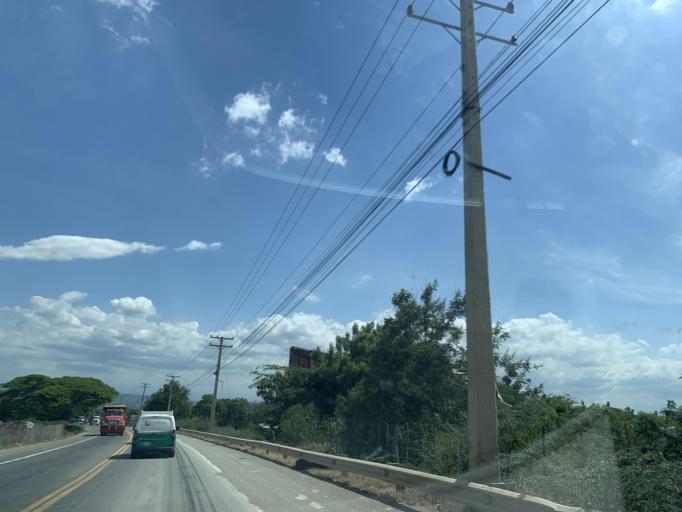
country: DO
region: Santiago
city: Villa Bisono
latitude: 19.5703
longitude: -70.8556
